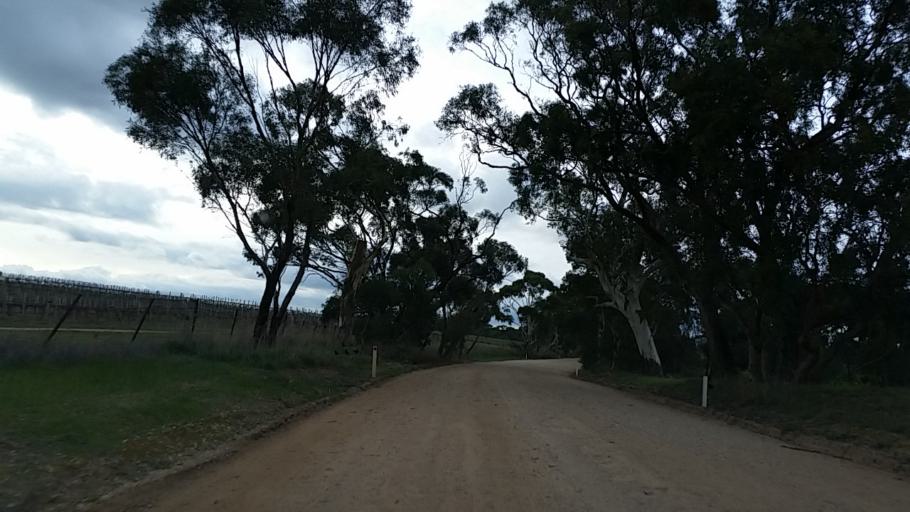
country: AU
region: South Australia
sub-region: Adelaide Hills
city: Woodside
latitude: -34.9437
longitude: 139.0126
